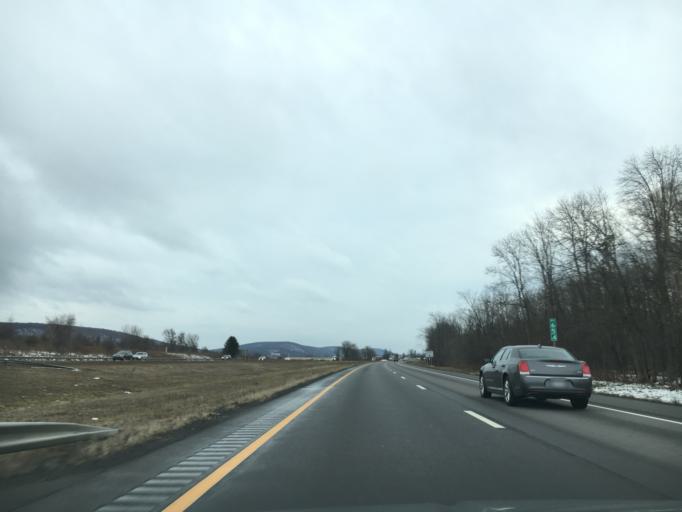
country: US
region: New York
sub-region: Cortland County
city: Homer
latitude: 42.7758
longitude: -76.1273
